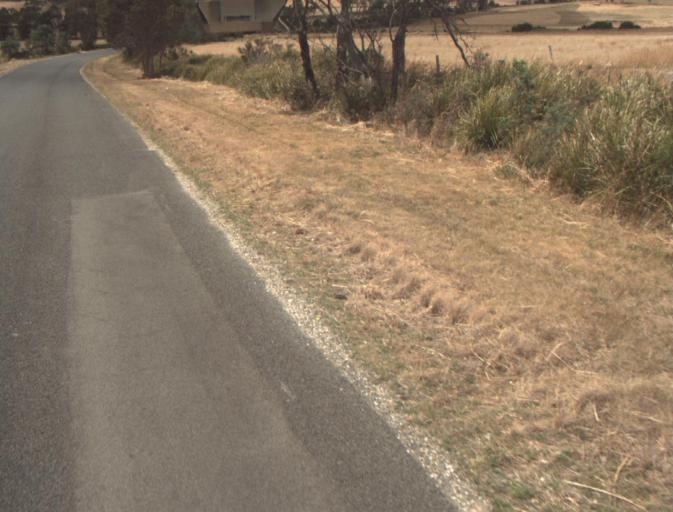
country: AU
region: Tasmania
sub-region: Launceston
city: Mayfield
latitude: -41.2030
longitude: 147.0797
